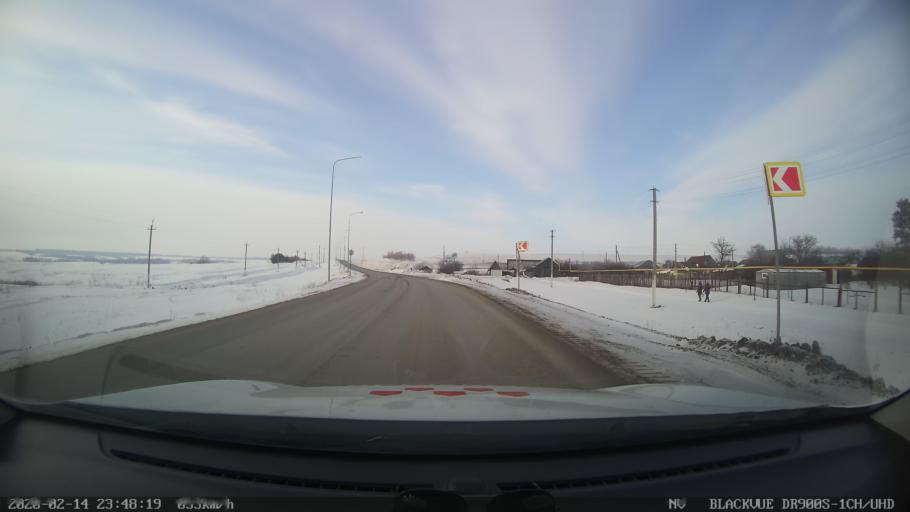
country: RU
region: Tatarstan
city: Kuybyshevskiy Zaton
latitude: 55.2473
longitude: 49.2040
